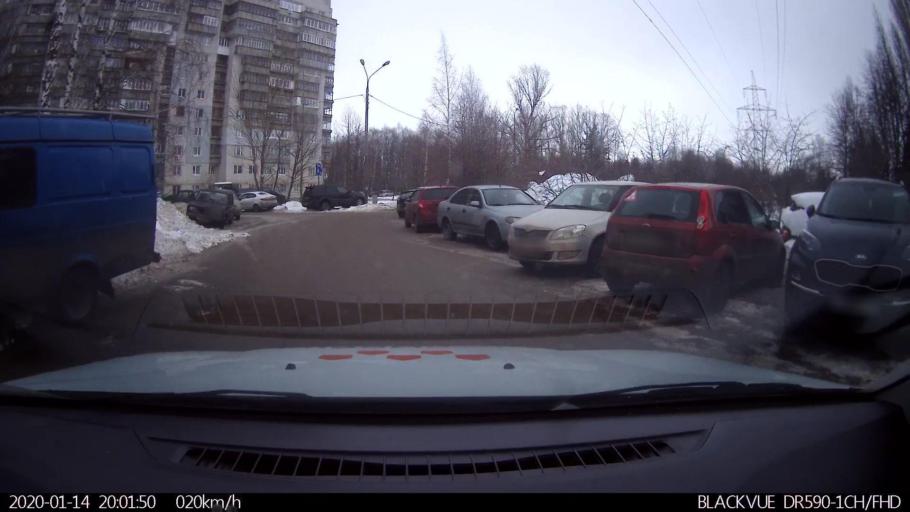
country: RU
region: Nizjnij Novgorod
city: Nizhniy Novgorod
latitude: 56.2328
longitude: 43.9428
